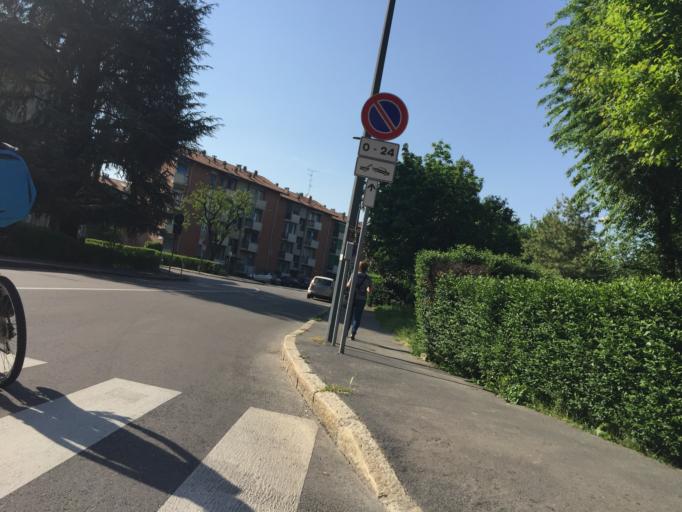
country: IT
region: Lombardy
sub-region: Citta metropolitana di Milano
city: Linate
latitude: 45.4603
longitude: 9.2466
